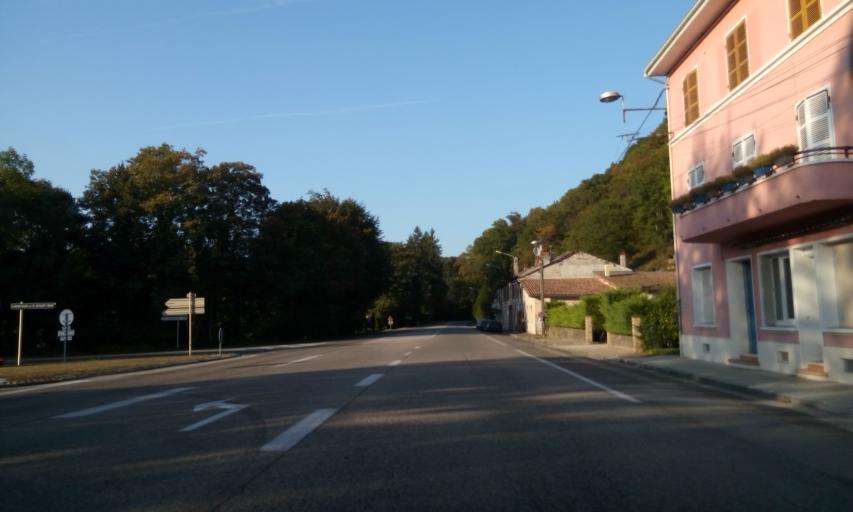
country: FR
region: Rhone-Alpes
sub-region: Departement de l'Ain
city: Neuville-sur-Ain
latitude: 46.0793
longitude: 5.3833
